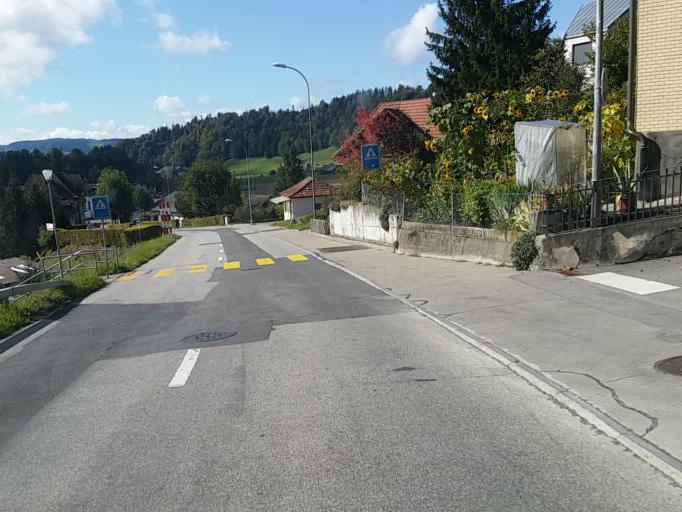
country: CH
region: Bern
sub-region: Emmental District
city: Sumiswald
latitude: 47.0270
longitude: 7.7399
